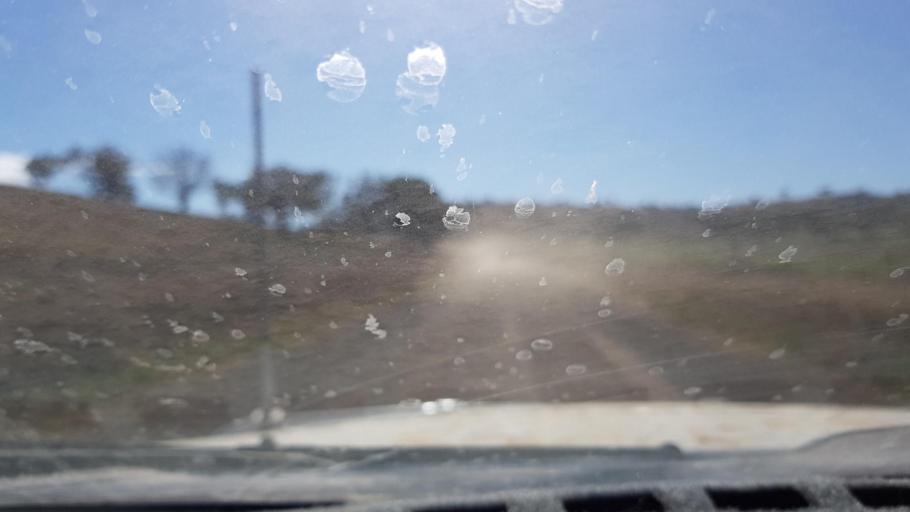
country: AU
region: New South Wales
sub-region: Narrabri
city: Blair Athol
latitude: -30.4410
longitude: 150.4554
